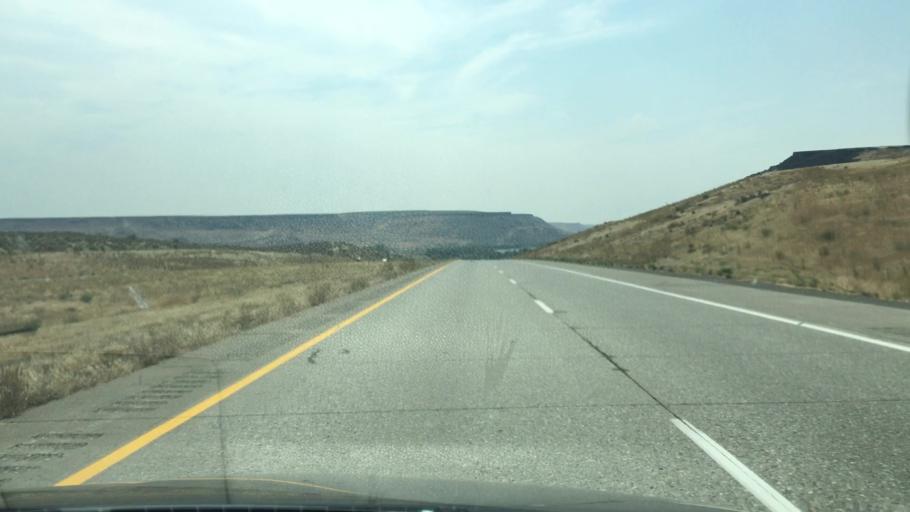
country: US
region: Idaho
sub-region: Elmore County
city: Glenns Ferry
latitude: 42.9614
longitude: -115.3398
